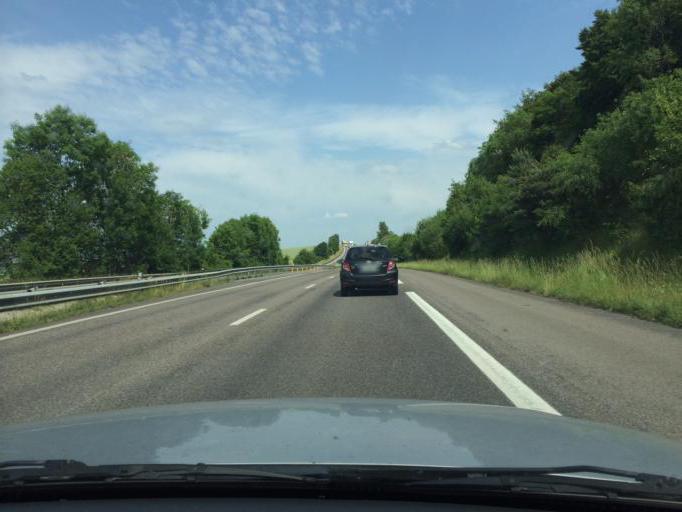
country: FR
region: Lorraine
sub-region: Departement de la Meuse
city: Lerouville
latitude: 48.7046
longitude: 5.5114
